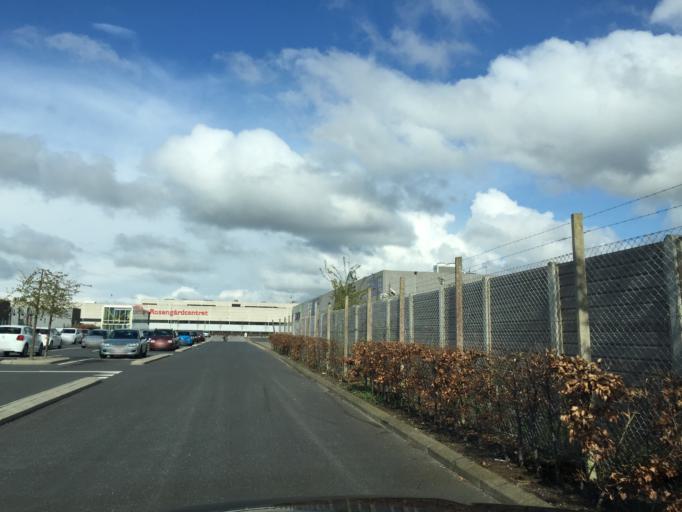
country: DK
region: South Denmark
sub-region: Odense Kommune
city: Neder Holluf
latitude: 55.3817
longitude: 10.4234
